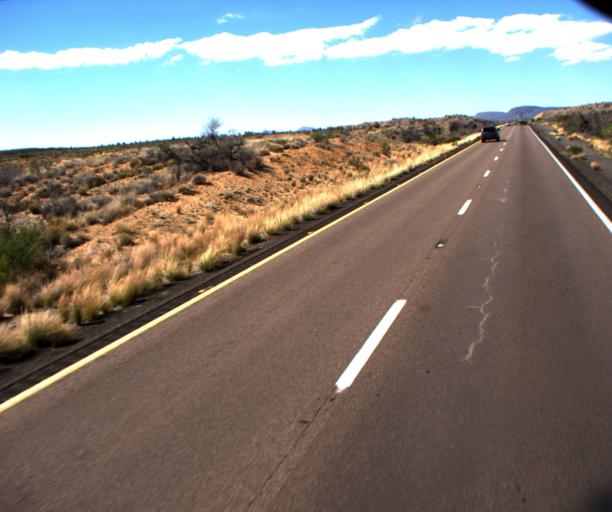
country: US
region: Arizona
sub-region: Mohave County
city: Kingman
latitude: 35.0692
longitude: -113.6651
